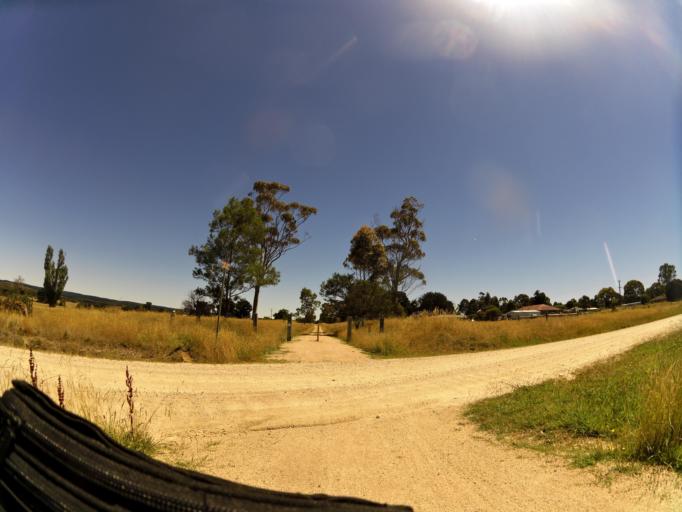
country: AU
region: Victoria
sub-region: Ballarat North
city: Delacombe
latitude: -37.6930
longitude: 143.6545
